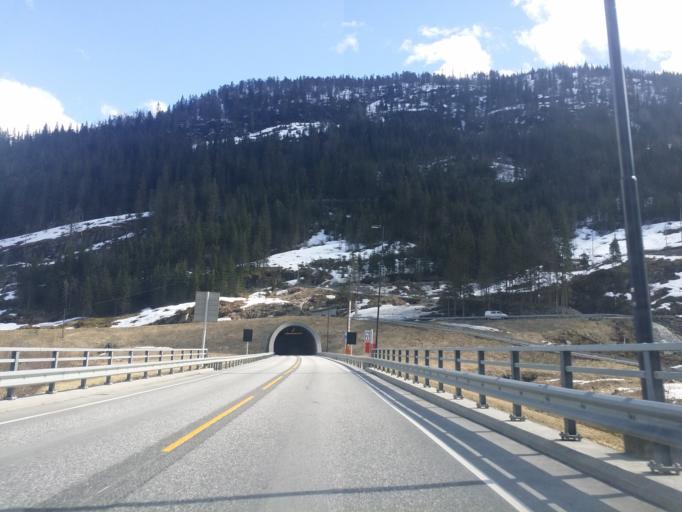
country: NO
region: Hordaland
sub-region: Granvin
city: Granvin
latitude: 60.5855
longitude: 6.6120
